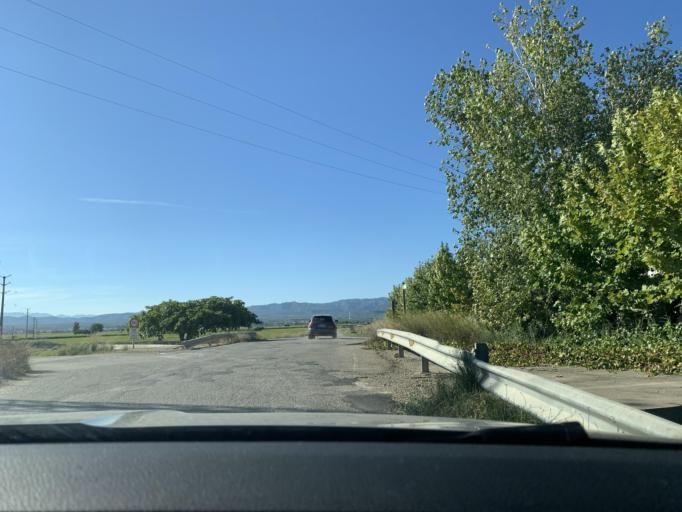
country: ES
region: Catalonia
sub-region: Provincia de Tarragona
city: Deltebre
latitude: 40.7579
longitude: 0.7116
